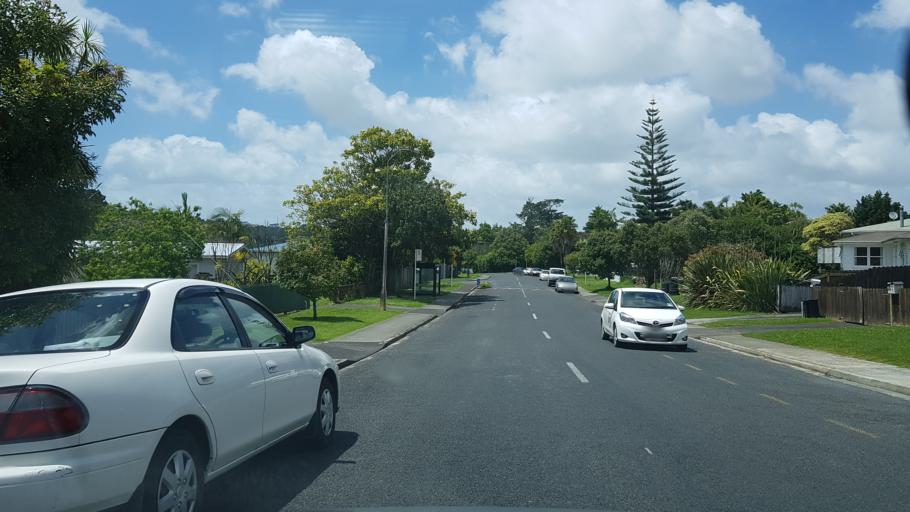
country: NZ
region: Auckland
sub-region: Auckland
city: North Shore
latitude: -36.7899
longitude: 174.7033
